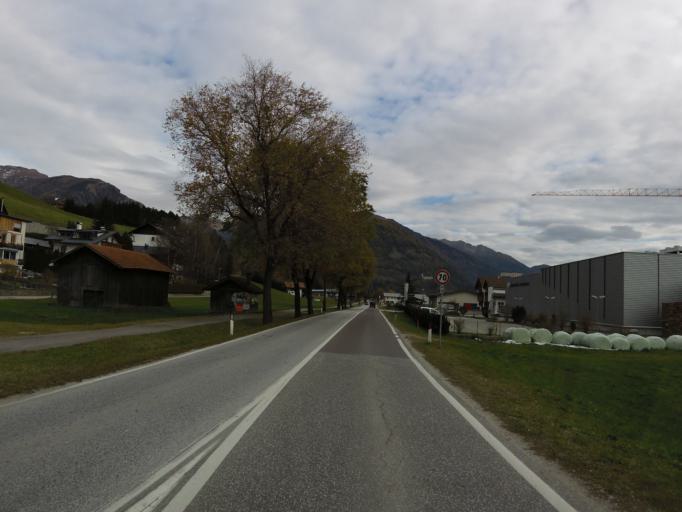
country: IT
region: Trentino-Alto Adige
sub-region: Bolzano
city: Vipiteno
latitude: 46.8870
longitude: 11.4184
